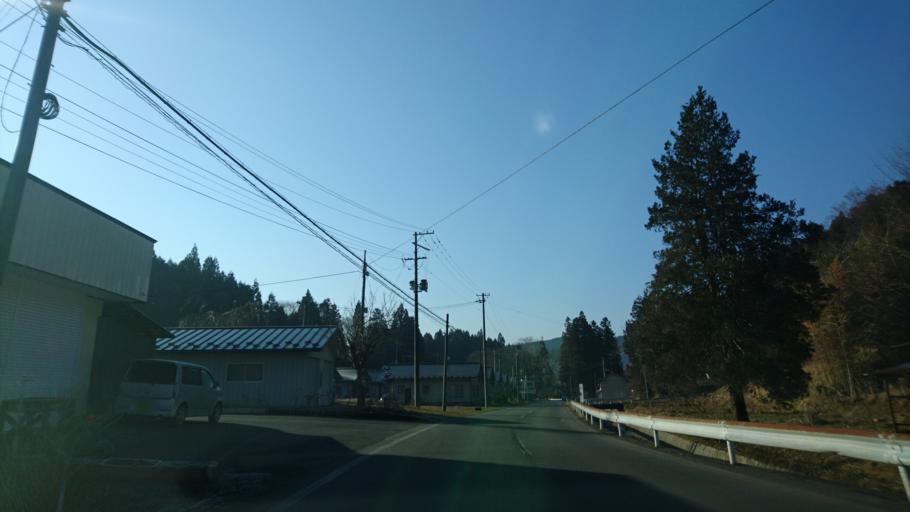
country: JP
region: Iwate
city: Ichinoseki
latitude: 38.9058
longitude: 141.2801
